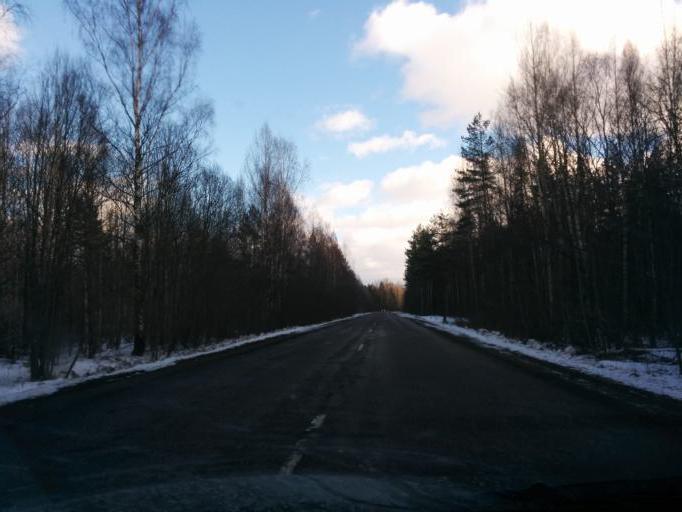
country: LV
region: Balvu Rajons
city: Balvi
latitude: 57.1760
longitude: 27.1206
